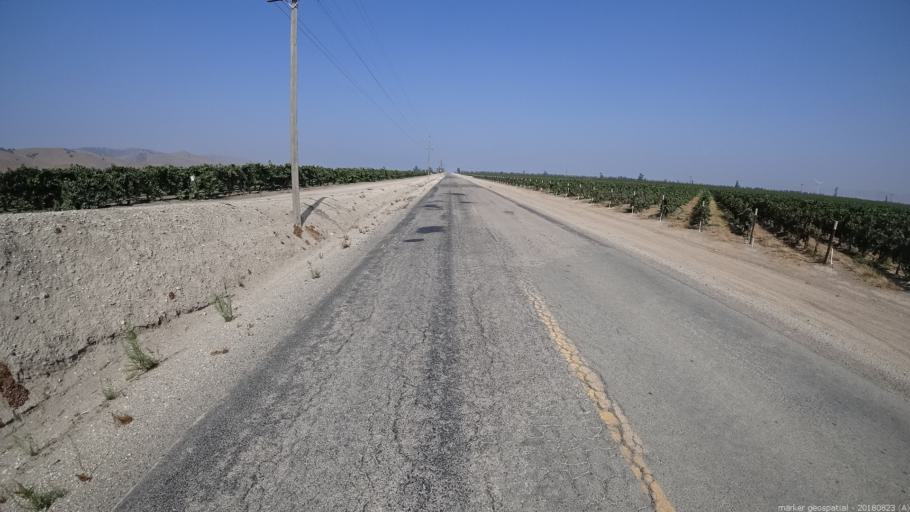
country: US
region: California
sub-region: Monterey County
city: King City
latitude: 36.2502
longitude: -121.1960
